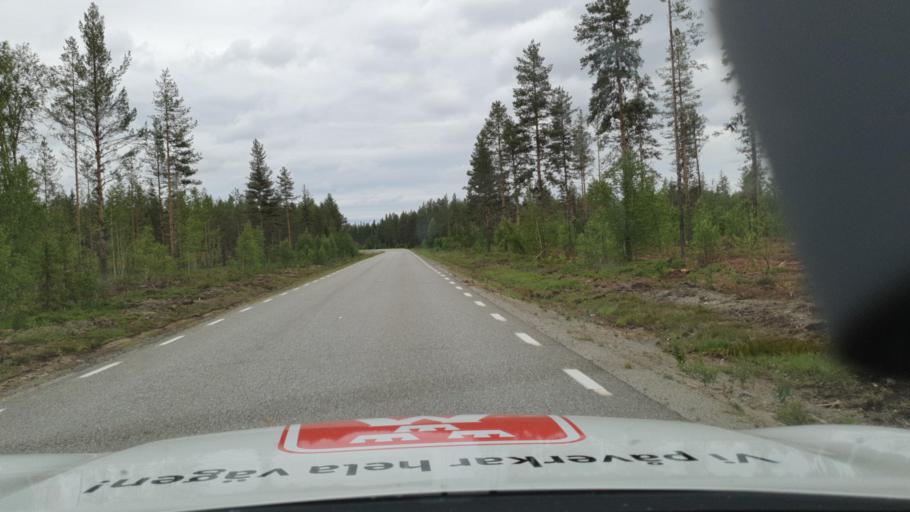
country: SE
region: Vaesterbotten
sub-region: Lycksele Kommun
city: Lycksele
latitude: 64.1983
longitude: 18.2989
